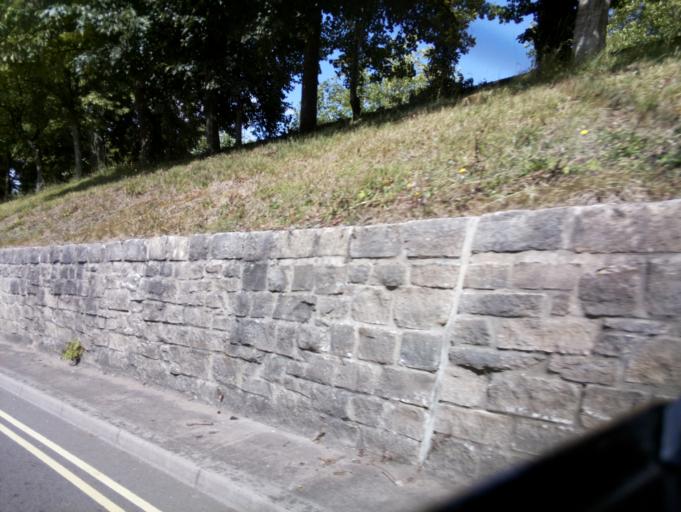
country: GB
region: England
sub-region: Dorset
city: Dorchester
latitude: 50.7159
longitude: -2.4417
